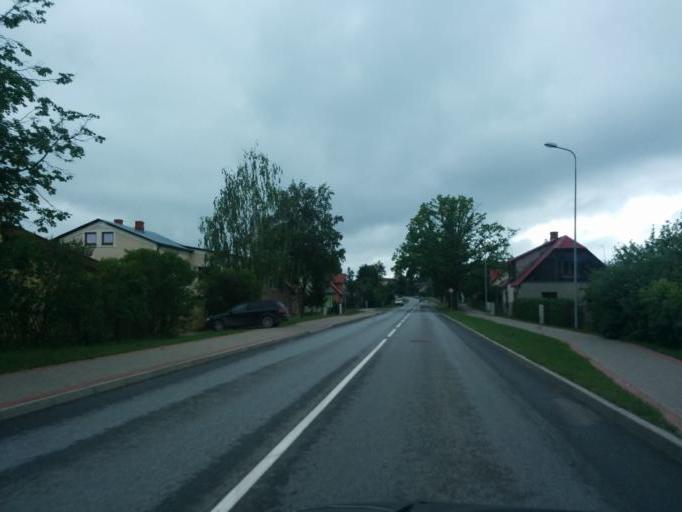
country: LV
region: Smiltene
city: Smiltene
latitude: 57.4289
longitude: 25.8908
